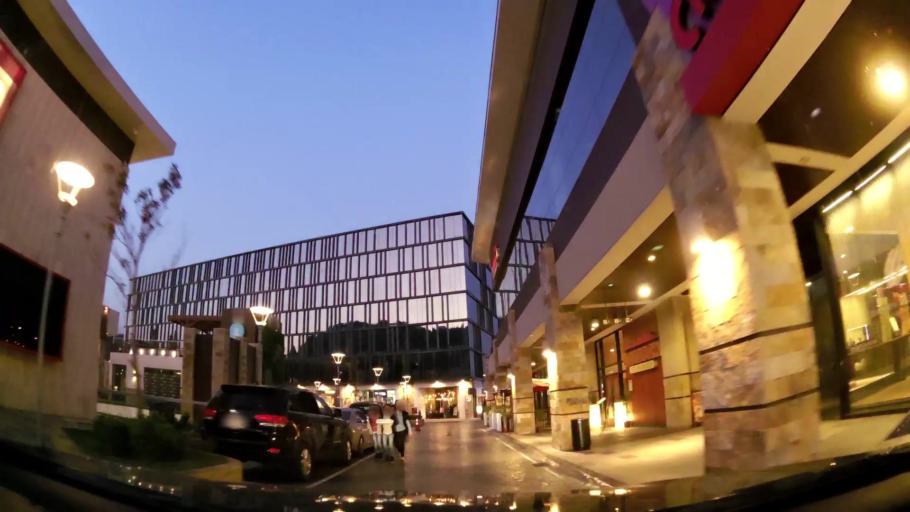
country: CL
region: Santiago Metropolitan
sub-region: Provincia de Santiago
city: Villa Presidente Frei, Nunoa, Santiago, Chile
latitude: -33.3570
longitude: -70.5400
